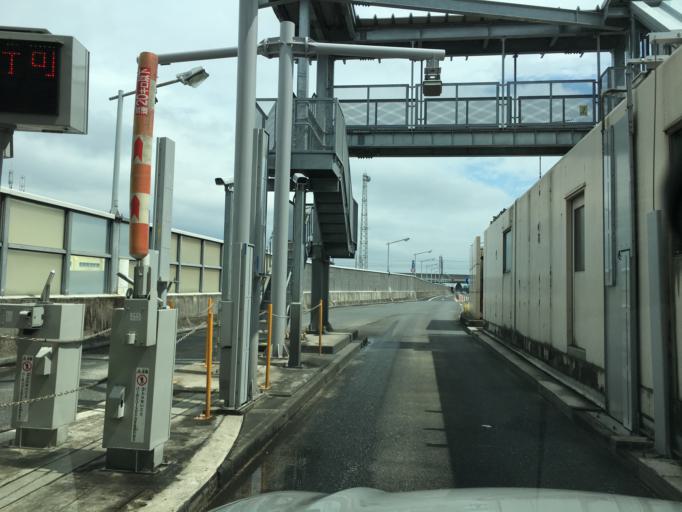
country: JP
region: Saitama
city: Shimotoda
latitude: 35.8290
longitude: 139.6536
